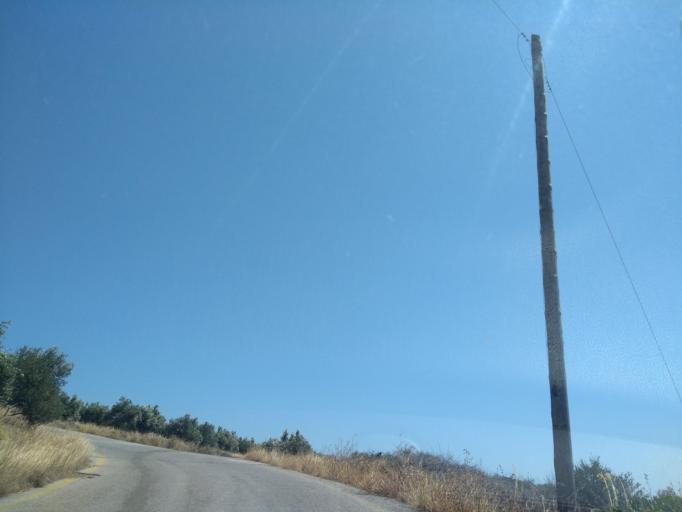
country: GR
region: Crete
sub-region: Nomos Chanias
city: Vryses
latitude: 35.3599
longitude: 23.5403
